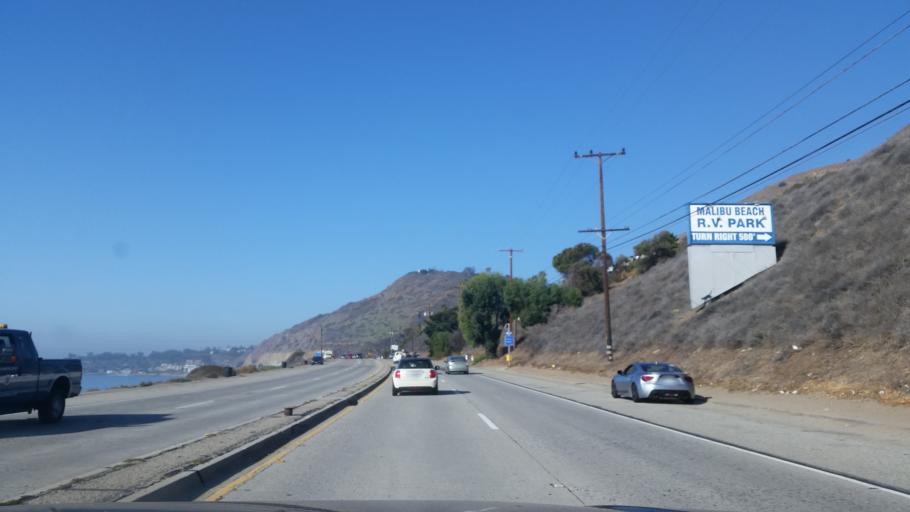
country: US
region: California
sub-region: Los Angeles County
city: Malibu Beach
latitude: 34.0335
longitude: -118.7357
